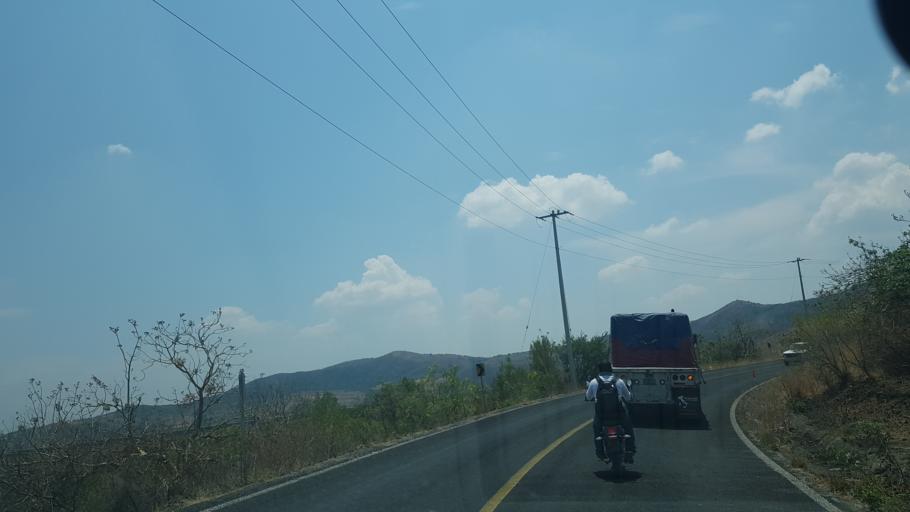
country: MX
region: Puebla
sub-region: Atzitzihuacan
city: Santiago Atzitzihuacan
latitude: 18.8324
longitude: -98.5881
